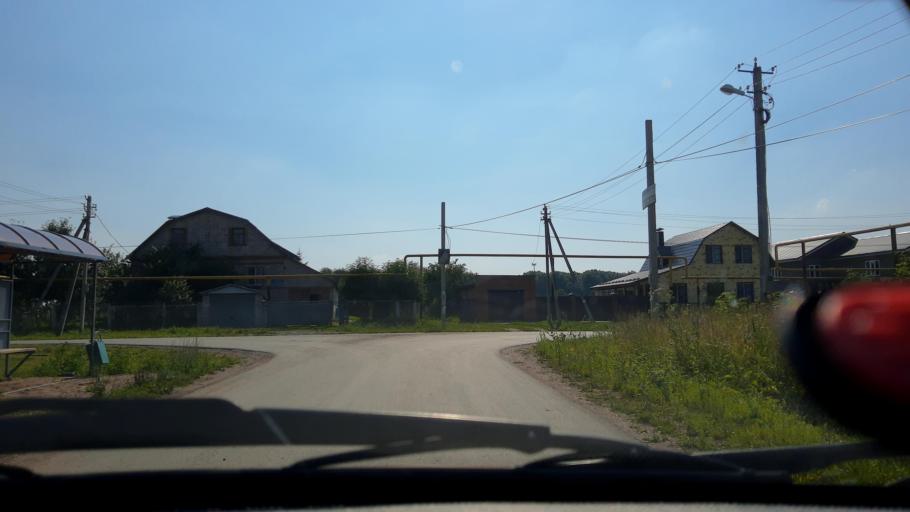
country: RU
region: Bashkortostan
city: Kabakovo
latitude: 54.7431
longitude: 56.1858
